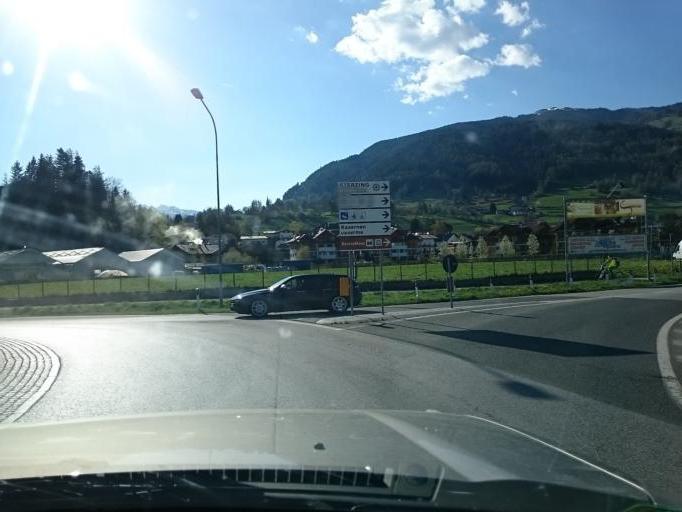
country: IT
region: Trentino-Alto Adige
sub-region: Bolzano
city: Vipiteno
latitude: 46.8889
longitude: 11.4310
